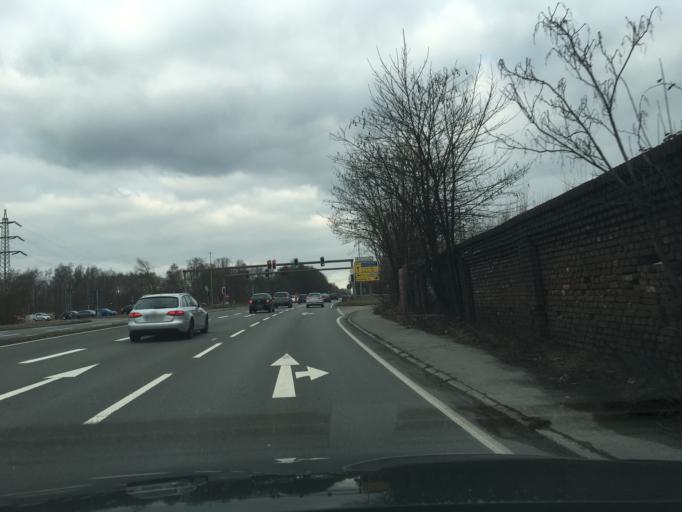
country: DE
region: North Rhine-Westphalia
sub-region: Regierungsbezirk Munster
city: Gladbeck
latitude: 51.5355
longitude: 6.9852
